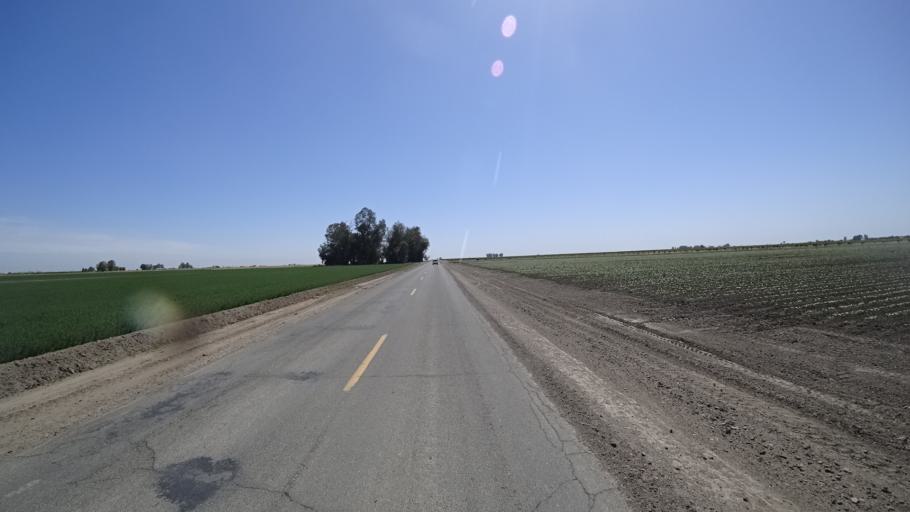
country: US
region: California
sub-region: Kings County
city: Stratford
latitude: 36.1895
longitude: -119.7943
